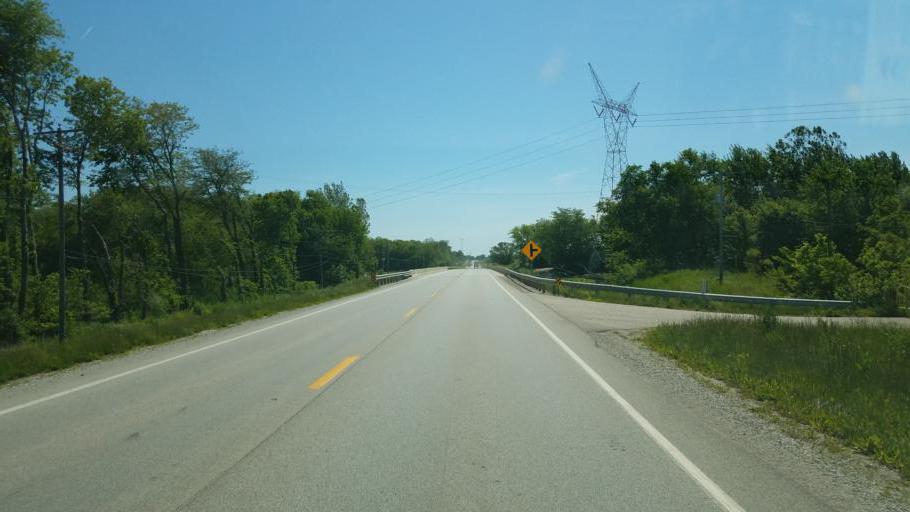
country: US
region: Illinois
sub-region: McLean County
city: Heyworth
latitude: 40.3121
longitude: -89.0162
